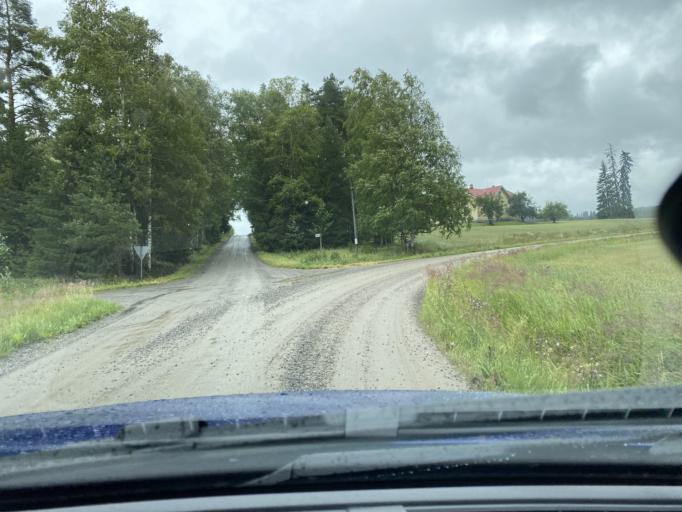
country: FI
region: Pirkanmaa
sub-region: Lounais-Pirkanmaa
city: Punkalaidun
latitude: 61.1504
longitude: 23.2265
